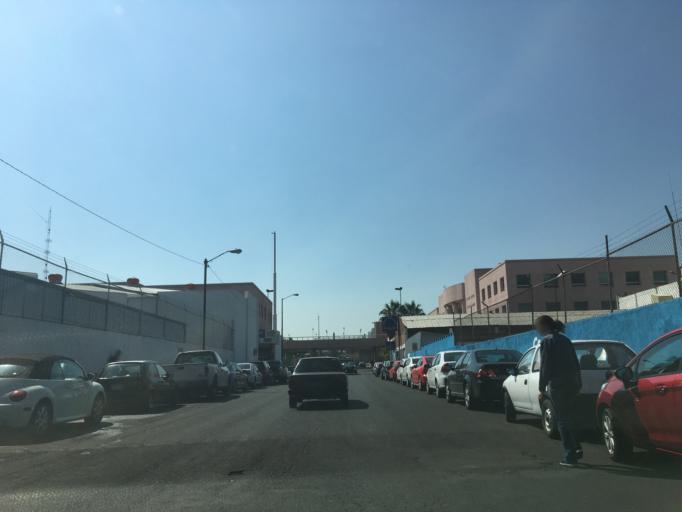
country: MX
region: Michoacan
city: Morelia
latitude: 19.6998
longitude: -101.2104
